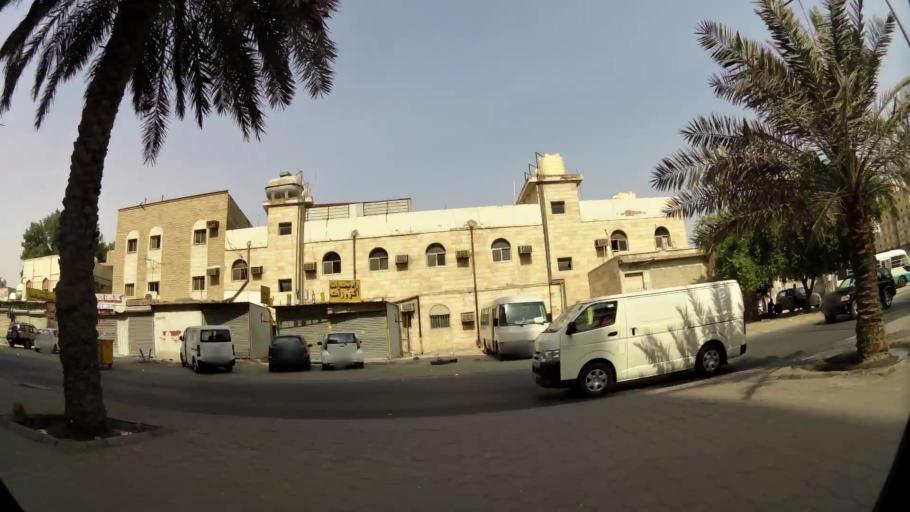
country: KW
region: Al Farwaniyah
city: Al Farwaniyah
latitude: 29.2592
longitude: 47.9320
